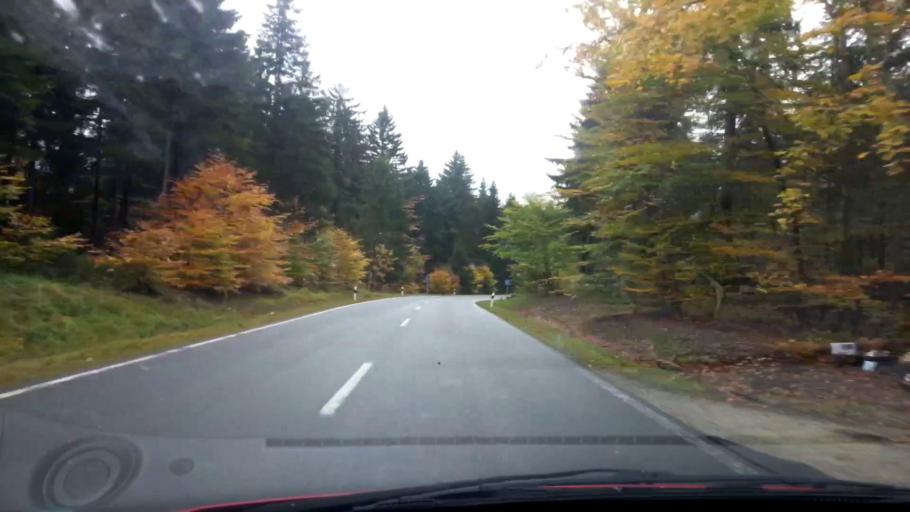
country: DE
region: Bavaria
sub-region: Upper Franconia
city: Fichtelberg
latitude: 50.0071
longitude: 11.8621
